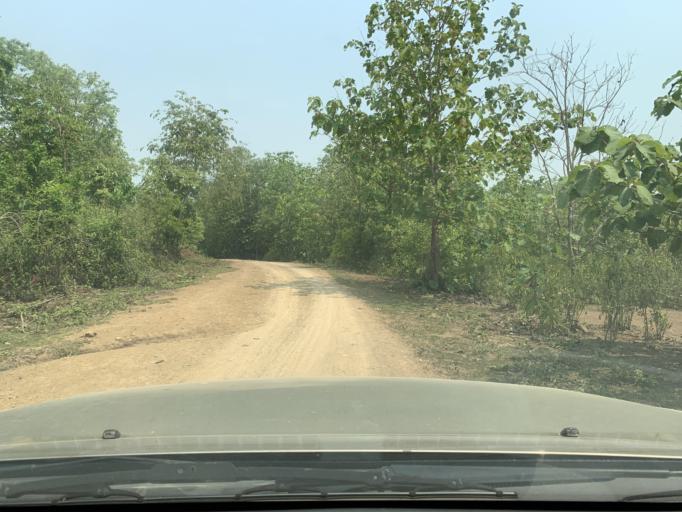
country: LA
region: Louangphabang
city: Louangphabang
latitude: 19.9408
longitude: 102.1332
